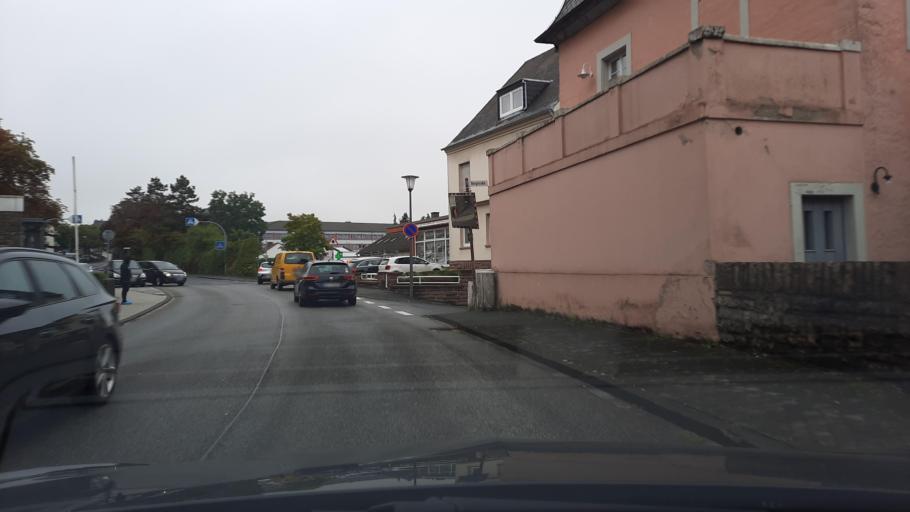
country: DE
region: Rheinland-Pfalz
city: Bitburg
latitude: 49.9713
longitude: 6.5273
